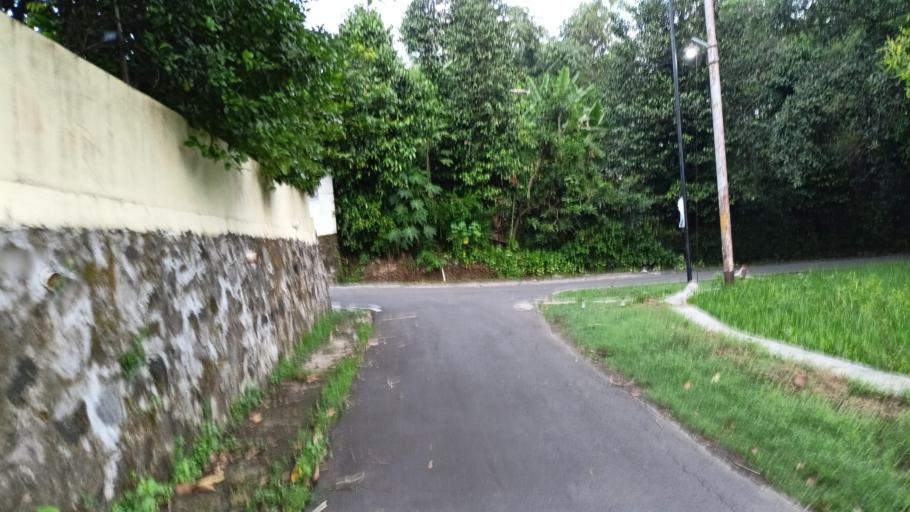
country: ID
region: Central Java
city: Jaten
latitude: -7.5941
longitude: 110.9152
